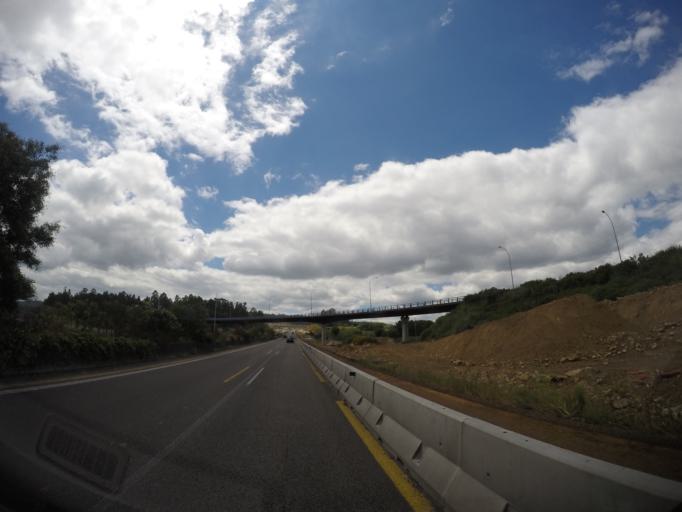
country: ES
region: Galicia
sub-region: Provincia da Coruna
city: Lousame
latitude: 42.8139
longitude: -8.7870
